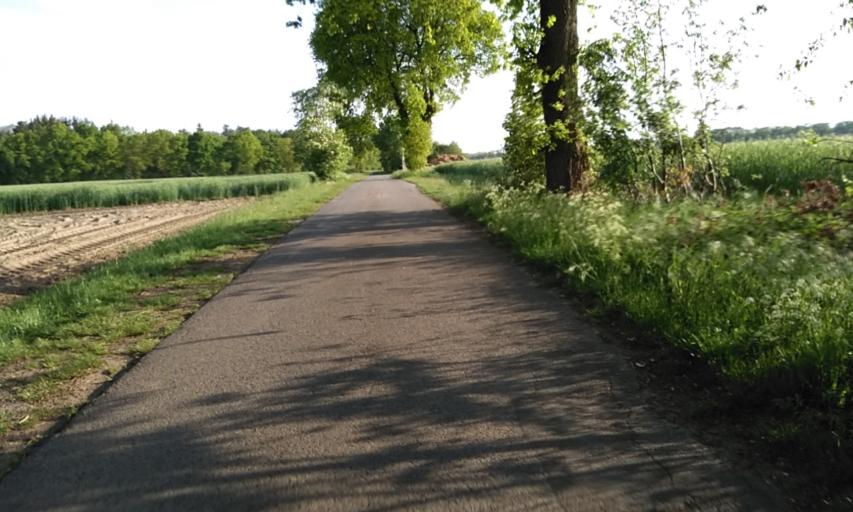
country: DE
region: Lower Saxony
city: Horneburg
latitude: 53.5017
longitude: 9.5640
